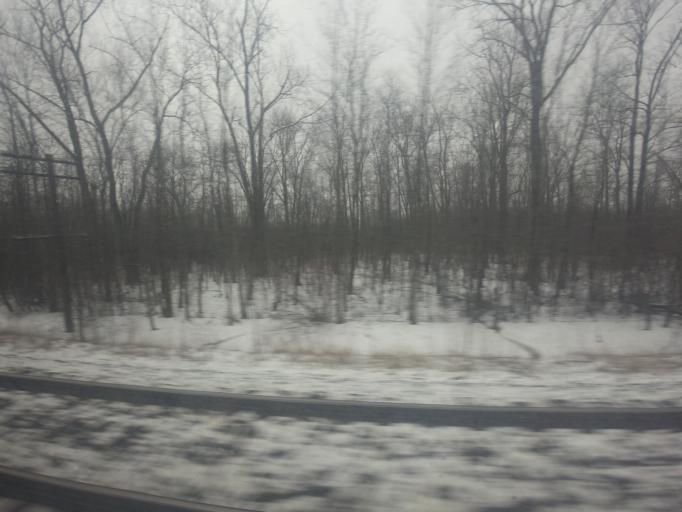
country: CA
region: Ontario
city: Quinte West
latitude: 44.1513
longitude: -77.4772
